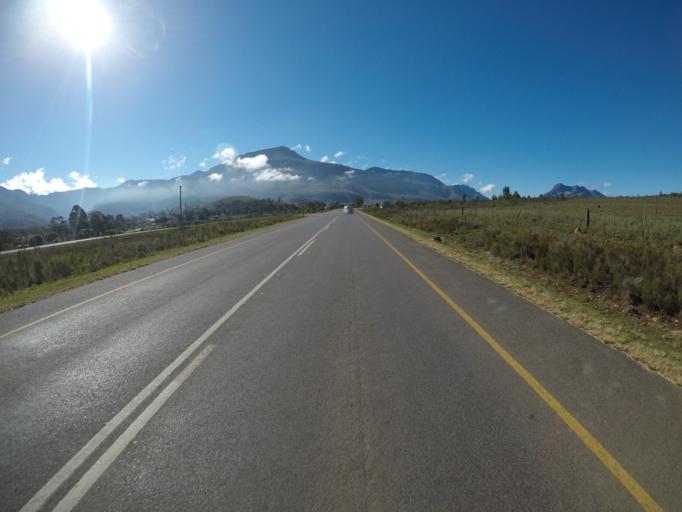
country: ZA
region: Western Cape
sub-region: Overberg District Municipality
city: Caledon
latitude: -34.0517
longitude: 19.5612
